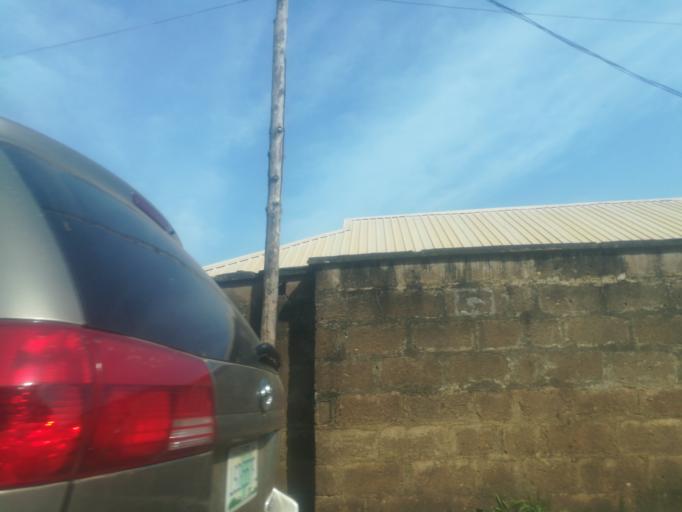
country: NG
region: Oyo
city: Ibadan
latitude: 7.3458
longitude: 3.8426
